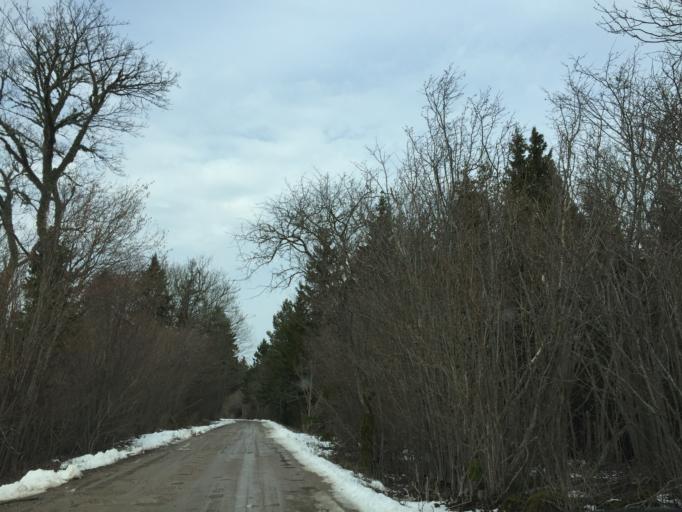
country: EE
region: Saare
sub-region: Kuressaare linn
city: Kuressaare
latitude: 58.4239
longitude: 22.1518
